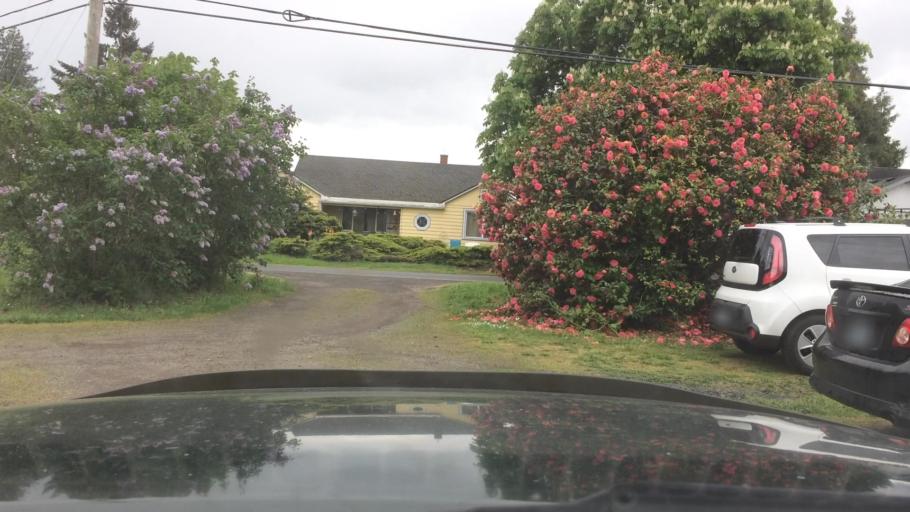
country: US
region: Oregon
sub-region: Lane County
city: Eugene
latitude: 44.1037
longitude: -123.1202
